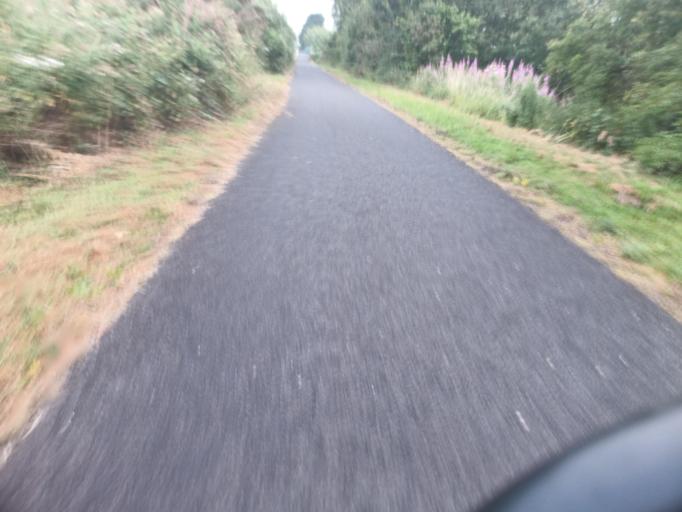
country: GB
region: Northern Ireland
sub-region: Ards District
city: Comber
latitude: 54.5670
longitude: -5.7665
